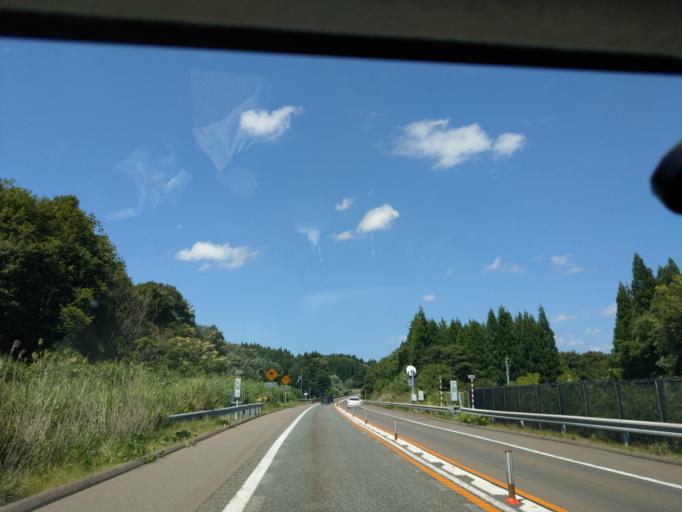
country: JP
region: Akita
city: Akita
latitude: 39.6754
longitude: 140.1864
